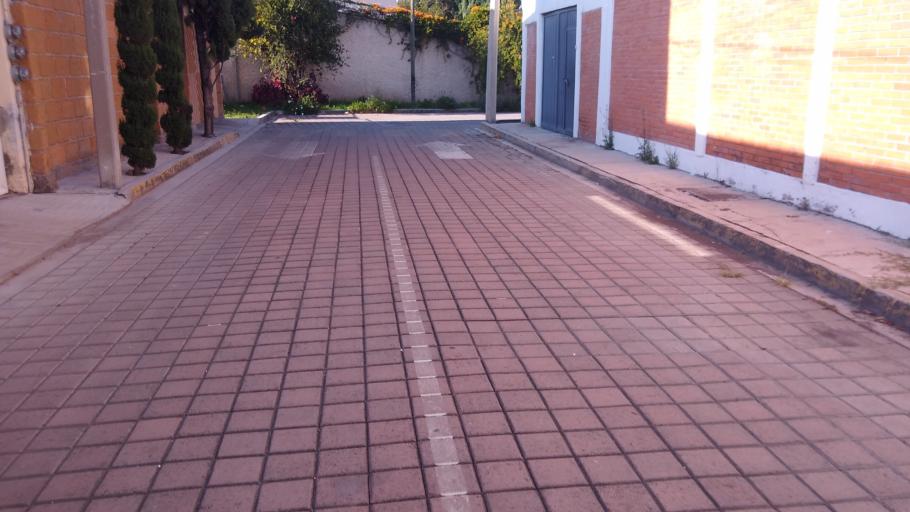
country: MX
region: Puebla
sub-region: San Pedro Cholula
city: Santiago Momoxpan
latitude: 19.0582
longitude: -98.2720
